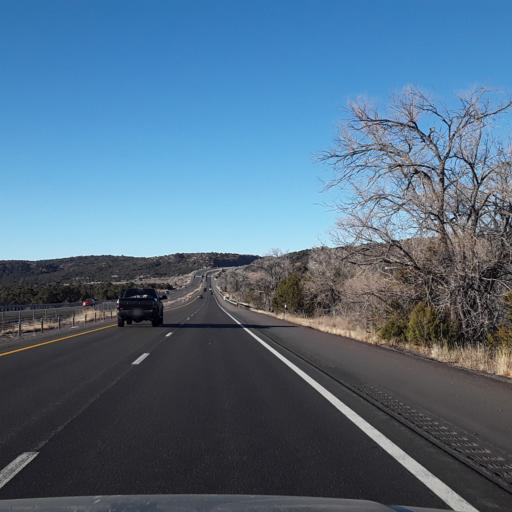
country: US
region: New Mexico
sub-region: Santa Fe County
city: Eldorado at Santa Fe
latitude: 35.5443
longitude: -105.8359
